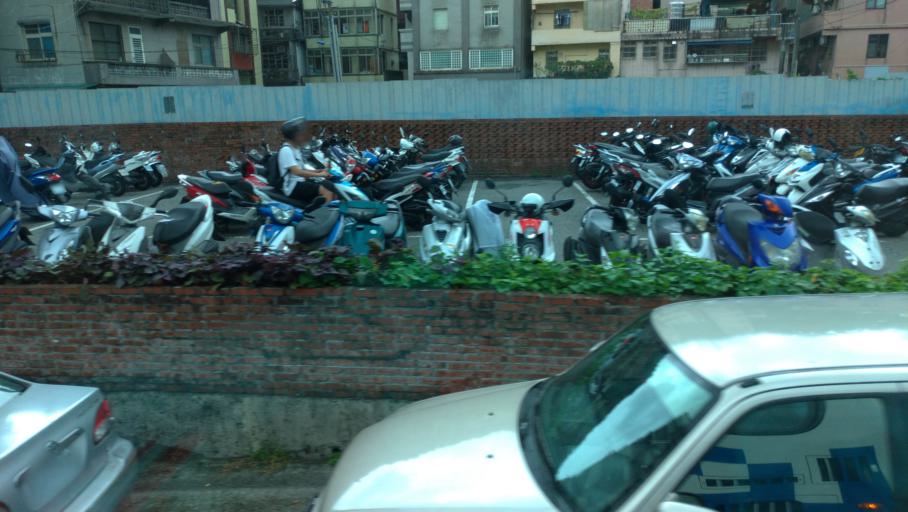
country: TW
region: Taiwan
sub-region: Keelung
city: Keelung
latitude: 25.1514
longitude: 121.7716
